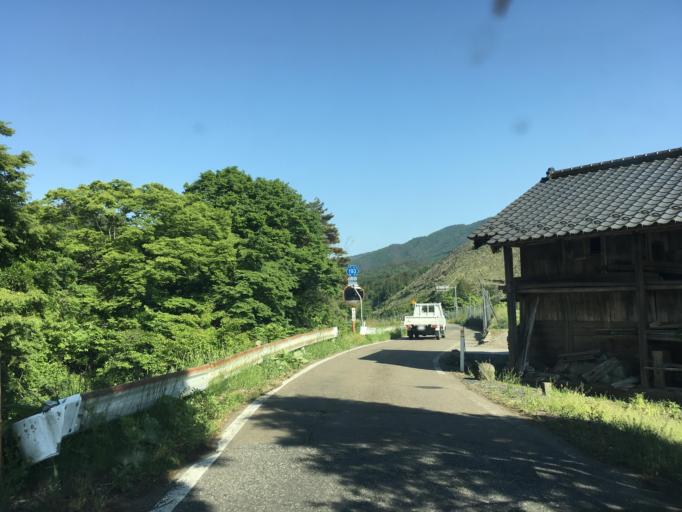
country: JP
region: Iwate
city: Kamaishi
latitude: 39.1967
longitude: 141.8356
